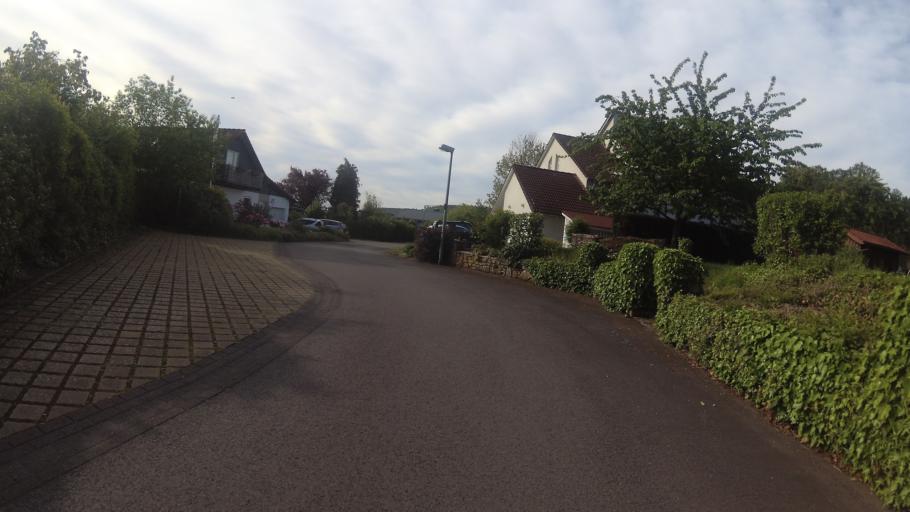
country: DE
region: Saarland
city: Merzig
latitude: 49.4221
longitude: 6.6269
